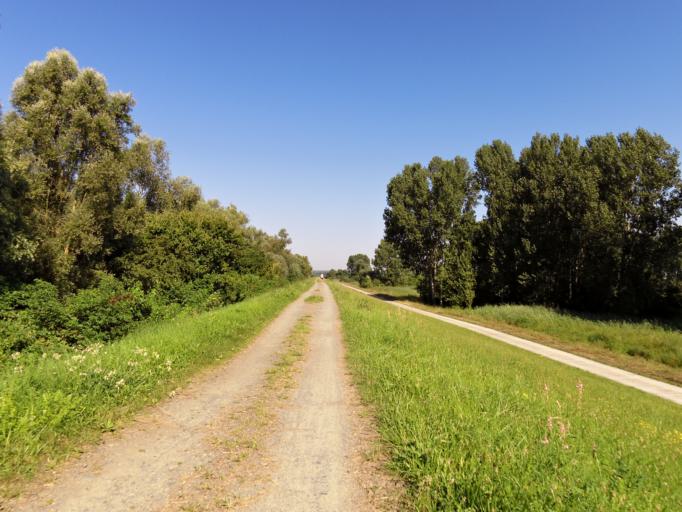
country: DE
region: Rheinland-Pfalz
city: Oppenheim
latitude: 49.8553
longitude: 8.3902
